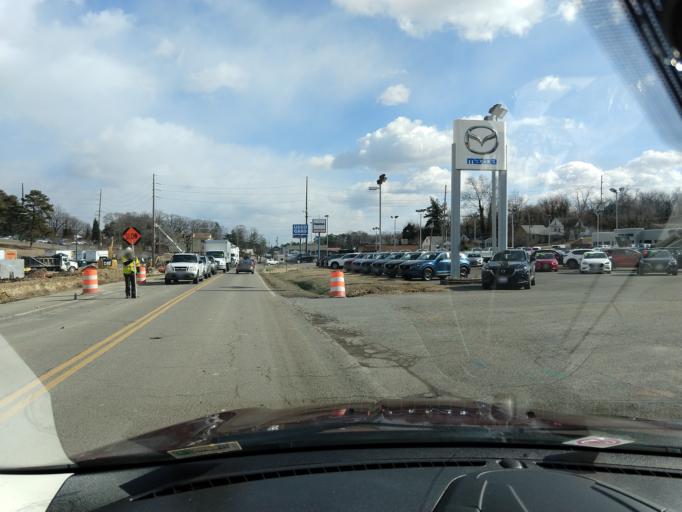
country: US
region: Virginia
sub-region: City of Salem
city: Salem
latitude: 37.2949
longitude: -80.0455
